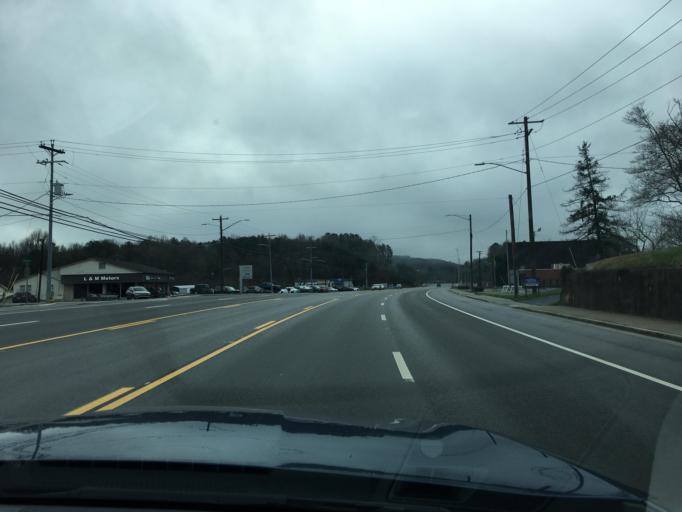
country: US
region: Tennessee
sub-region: McMinn County
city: Athens
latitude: 35.4280
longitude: -84.5832
